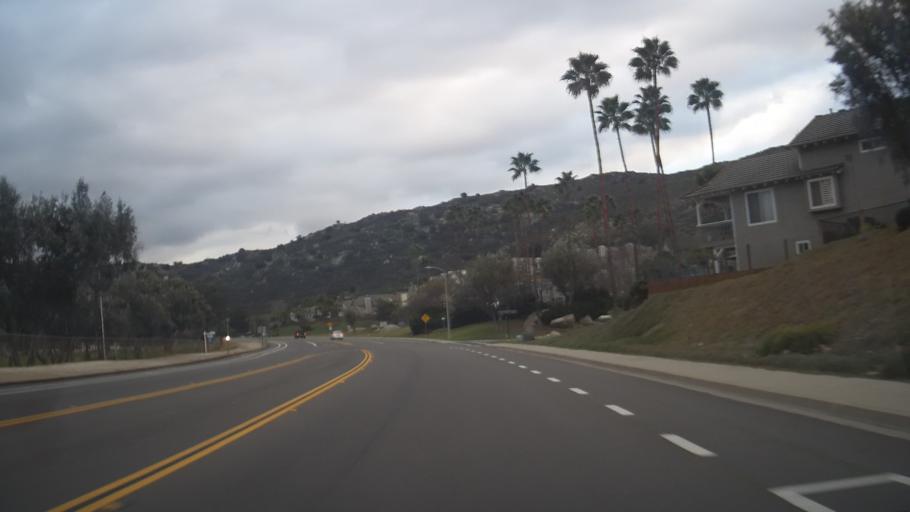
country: US
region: California
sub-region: San Diego County
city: Granite Hills
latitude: 32.7773
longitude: -116.8884
